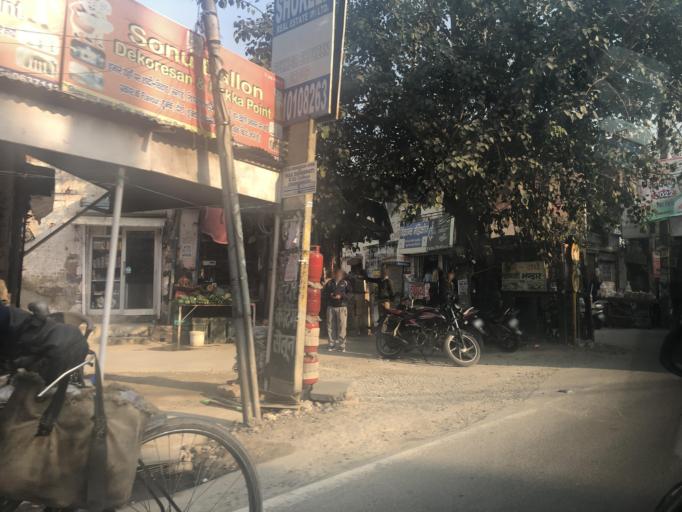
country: IN
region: Haryana
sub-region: Gurgaon
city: Gurgaon
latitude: 28.5616
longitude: 77.0020
